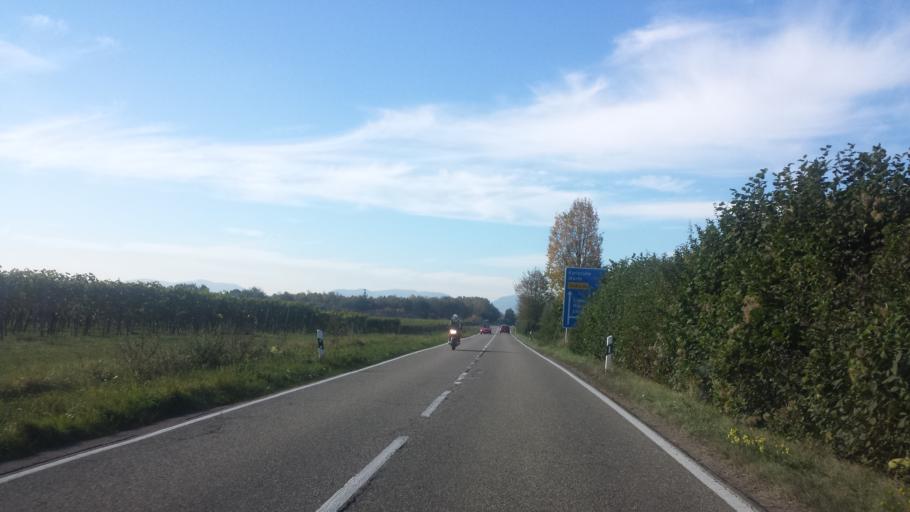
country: DE
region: Rheinland-Pfalz
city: Insheim
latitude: 49.1551
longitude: 8.1611
